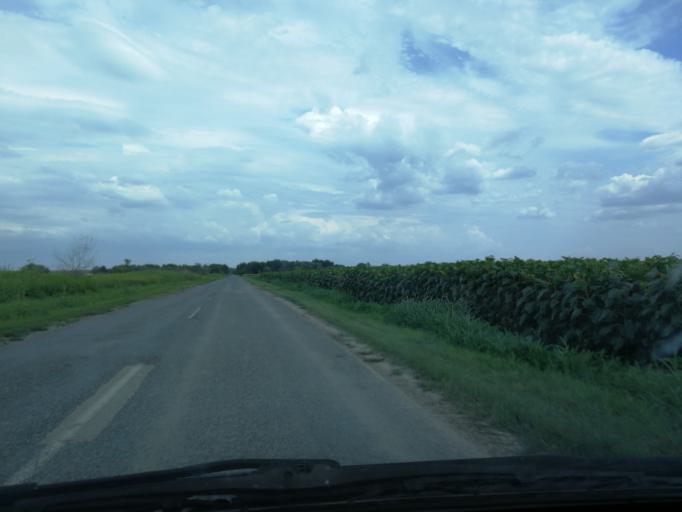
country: HU
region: Bacs-Kiskun
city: Batya
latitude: 46.4439
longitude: 18.9949
